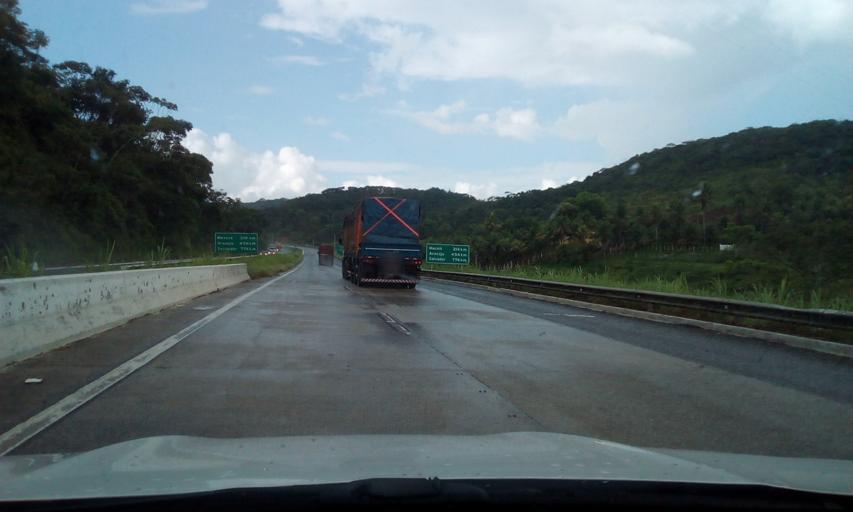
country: BR
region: Pernambuco
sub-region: Cabo De Santo Agostinho
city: Cabo
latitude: -8.3188
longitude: -35.1096
